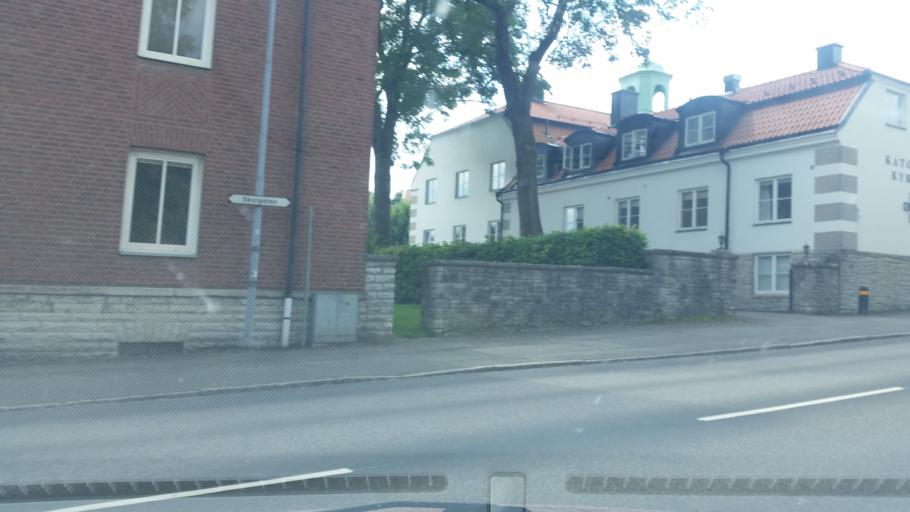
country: SE
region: Vaestra Goetaland
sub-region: Skovde Kommun
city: Skoevde
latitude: 58.3871
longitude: 13.8435
